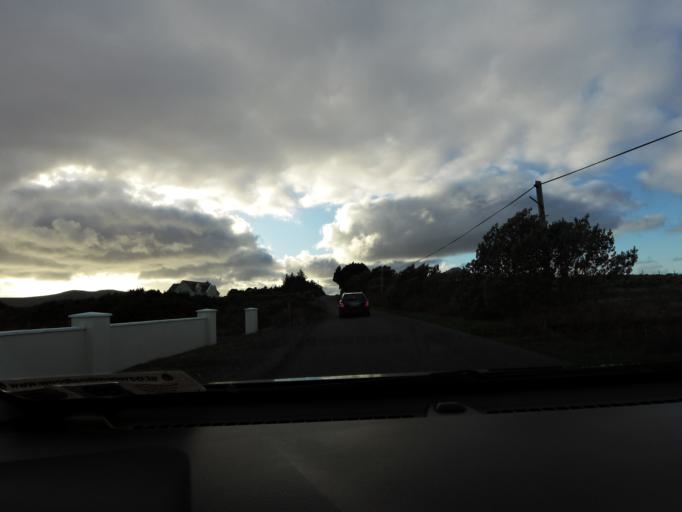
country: IE
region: Connaught
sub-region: Maigh Eo
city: Belmullet
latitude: 53.9955
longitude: -9.9530
